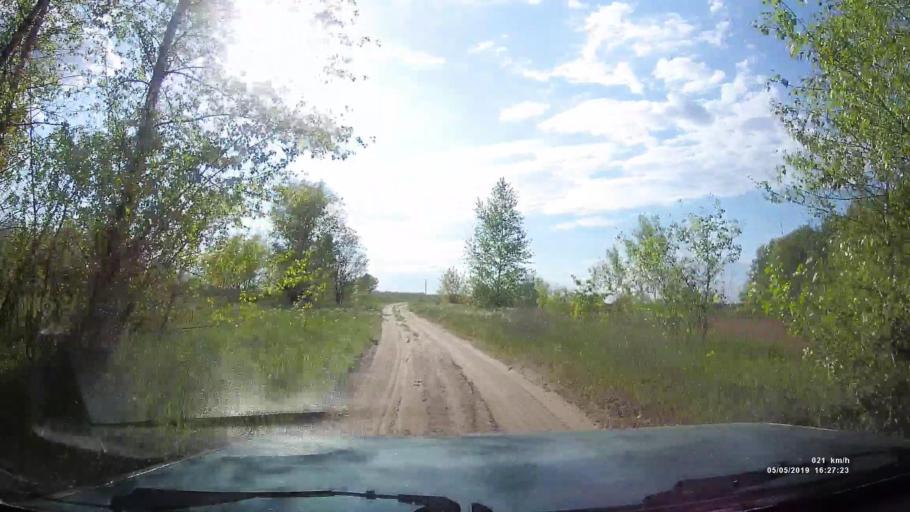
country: RU
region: Rostov
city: Ust'-Donetskiy
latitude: 47.7649
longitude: 41.0188
